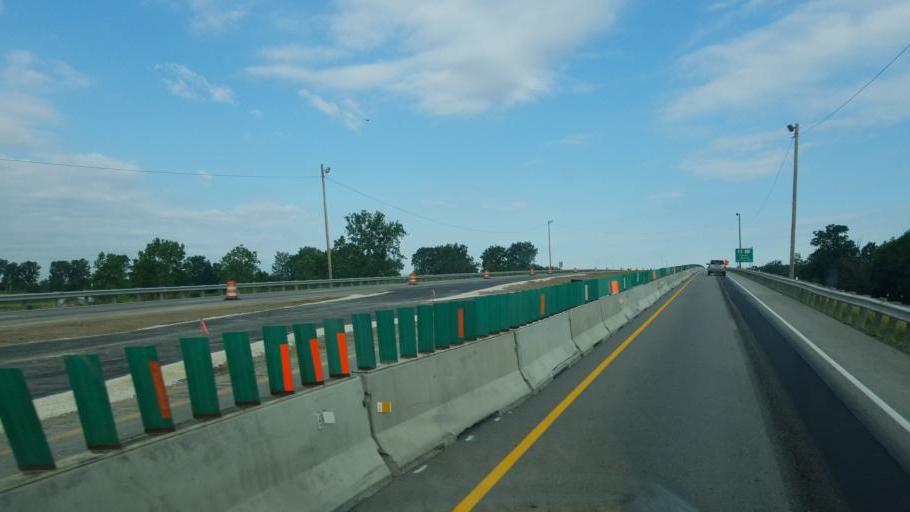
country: US
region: Ohio
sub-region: Wyandot County
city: Carey
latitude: 40.9366
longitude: -83.3908
